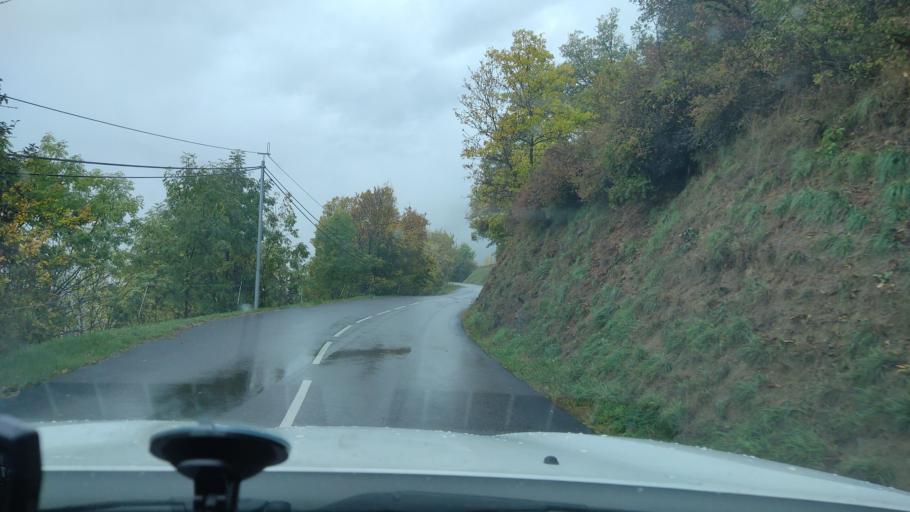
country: FR
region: Rhone-Alpes
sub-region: Departement de la Savoie
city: Les Allues
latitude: 45.4591
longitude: 6.5829
